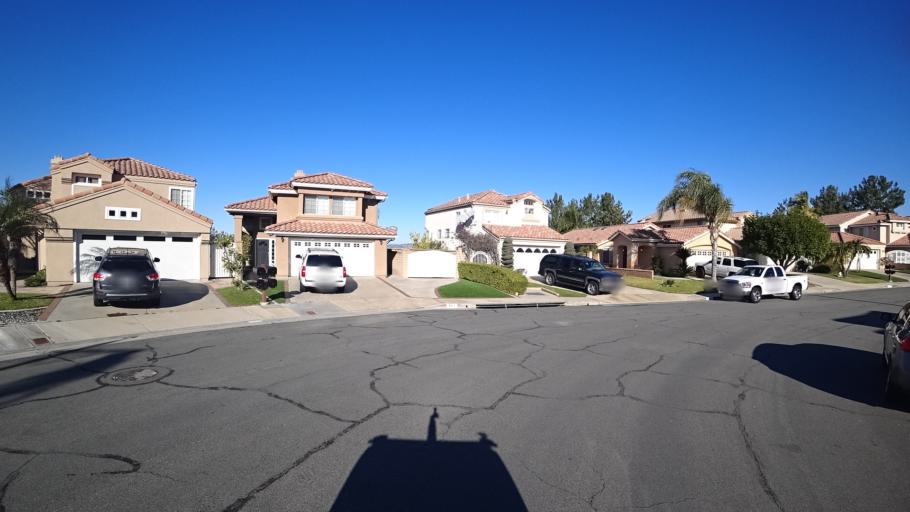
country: US
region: California
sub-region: Orange County
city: Yorba Linda
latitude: 33.8634
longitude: -117.7354
